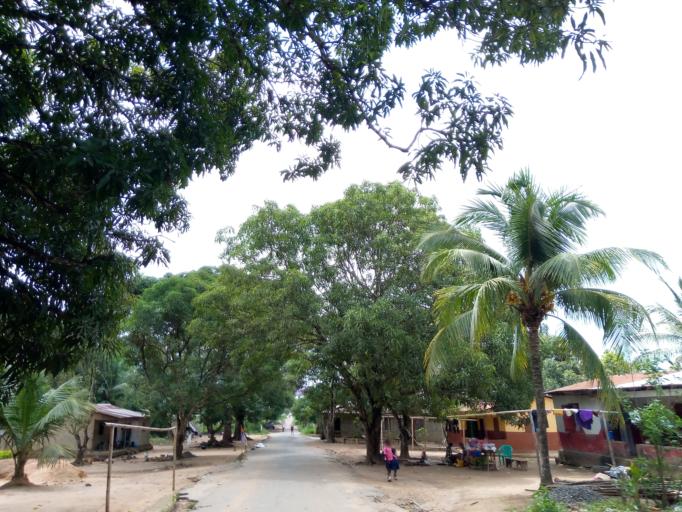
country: SL
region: Western Area
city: Waterloo
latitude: 8.3905
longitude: -12.9469
